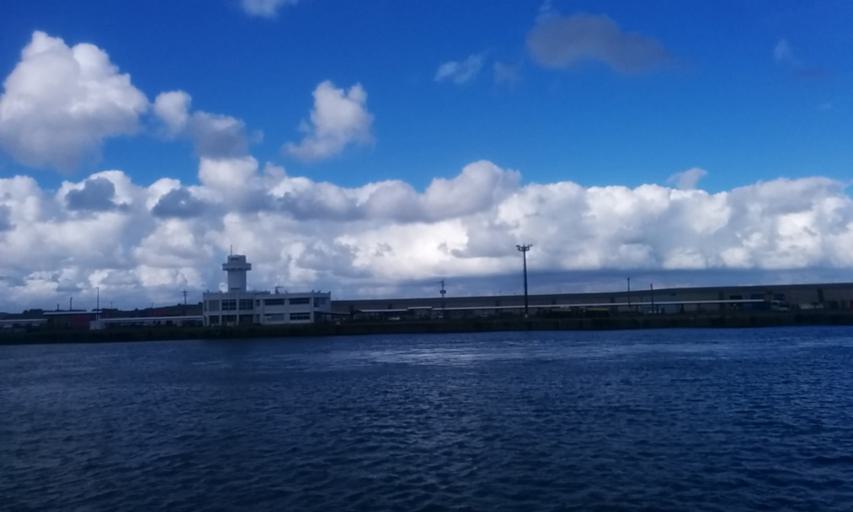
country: JP
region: Kagoshima
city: Nishinoomote
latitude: 30.4304
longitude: 130.5726
